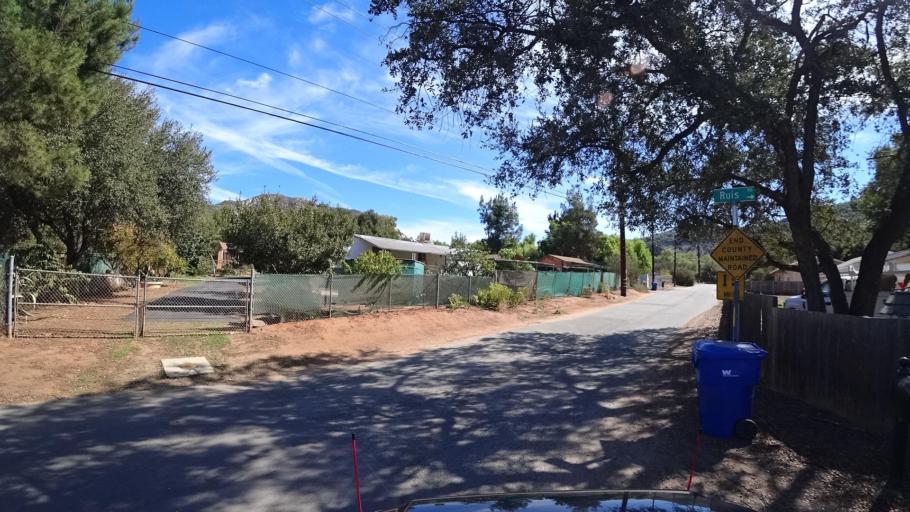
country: US
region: California
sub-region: San Diego County
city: Crest
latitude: 32.8374
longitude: -116.8735
